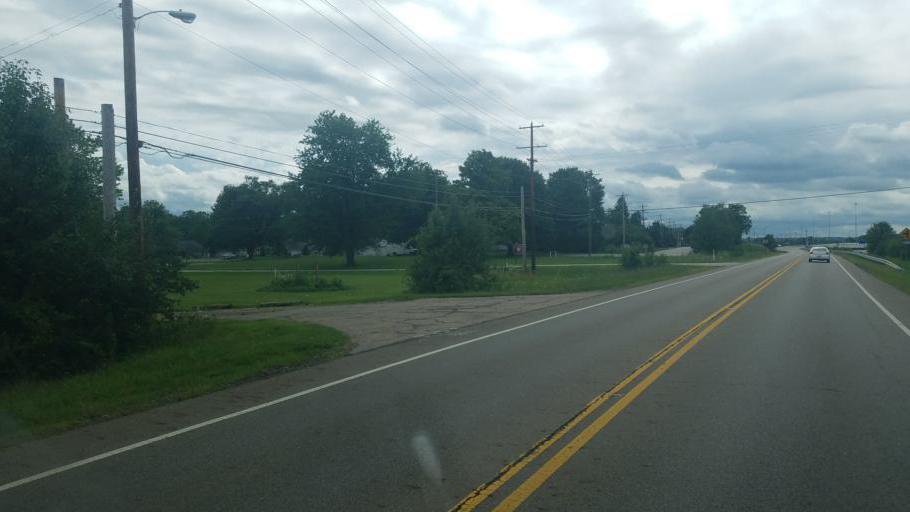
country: US
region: Ohio
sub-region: Franklin County
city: Huber Ridge
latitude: 40.0794
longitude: -82.8726
